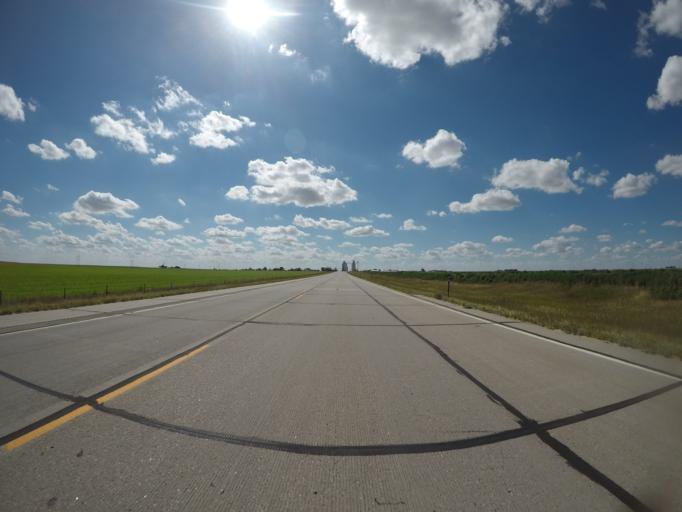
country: US
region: Colorado
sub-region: Phillips County
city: Holyoke
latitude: 40.6102
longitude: -102.4573
